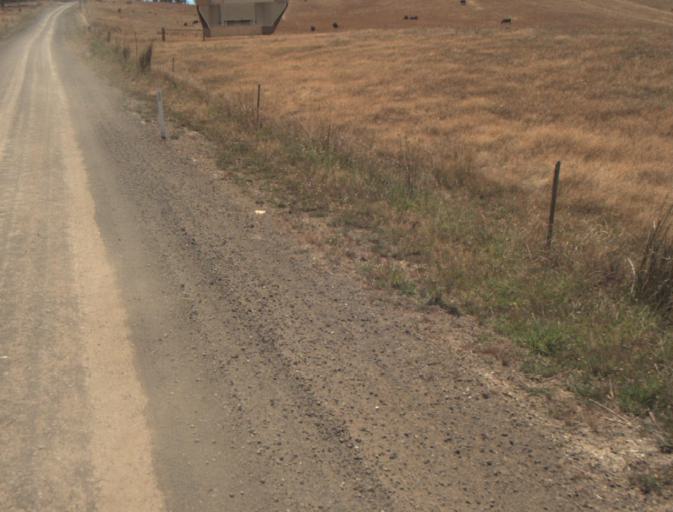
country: AU
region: Tasmania
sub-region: Launceston
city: Mayfield
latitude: -41.2519
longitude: 147.1339
